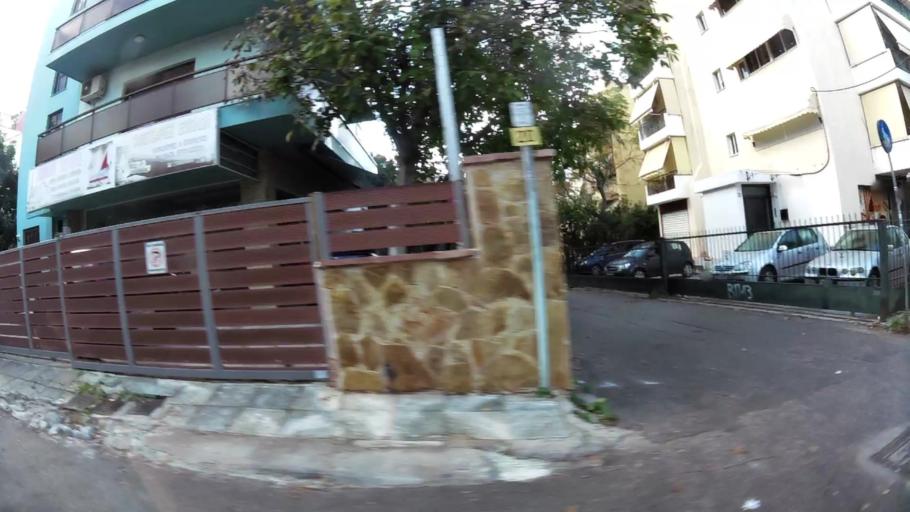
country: GR
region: Attica
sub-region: Nomarchia Athinas
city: Marousi
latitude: 38.0490
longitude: 23.8100
